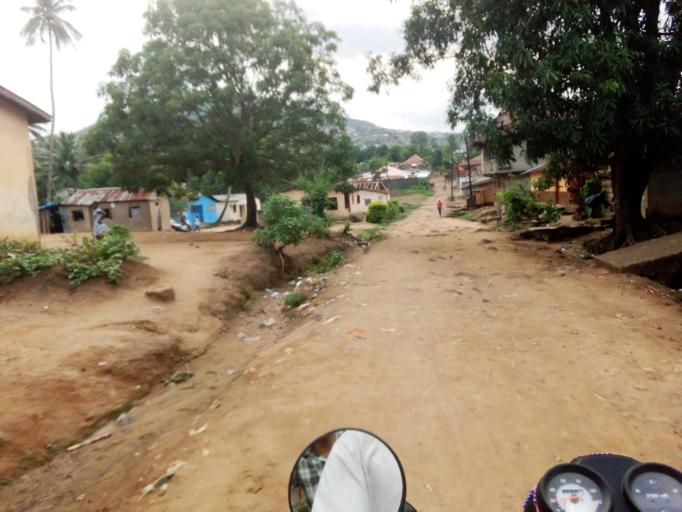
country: SL
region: Western Area
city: Waterloo
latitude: 8.3346
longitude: -13.0702
